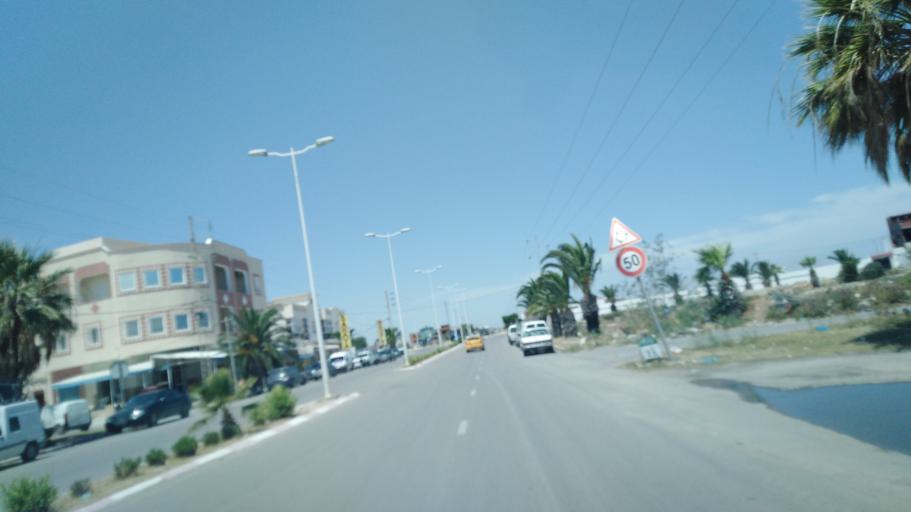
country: TN
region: Al Mahdiyah
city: Ksour Essaf
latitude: 35.4252
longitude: 10.9943
